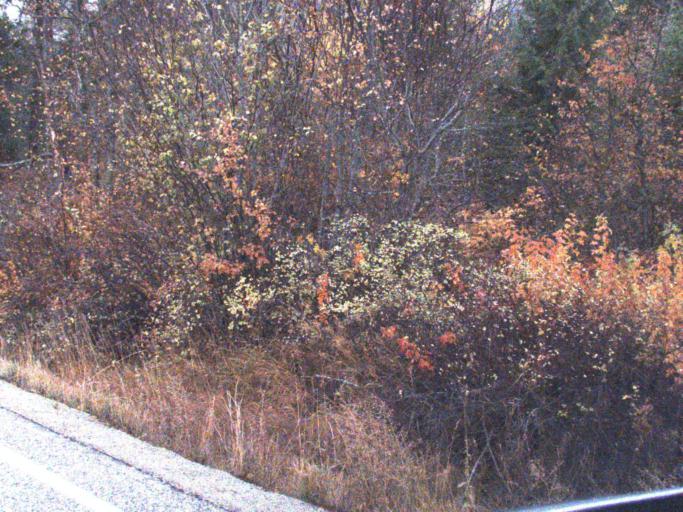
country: CA
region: British Columbia
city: Grand Forks
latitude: 48.9774
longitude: -118.2239
